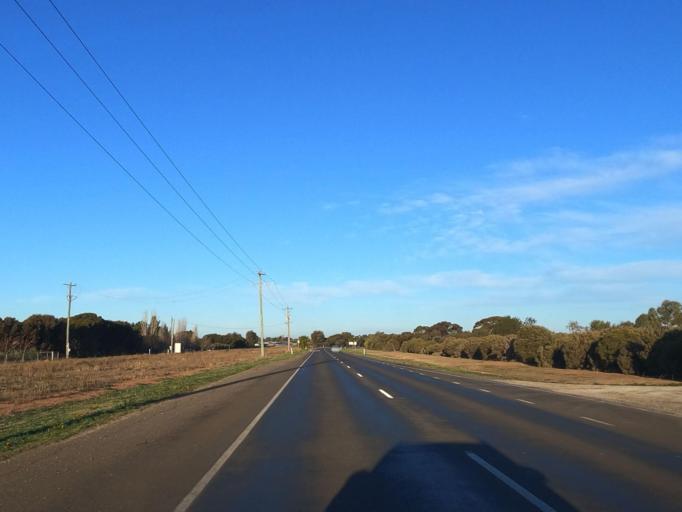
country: AU
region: Victoria
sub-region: Swan Hill
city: Swan Hill
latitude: -35.3361
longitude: 143.5348
